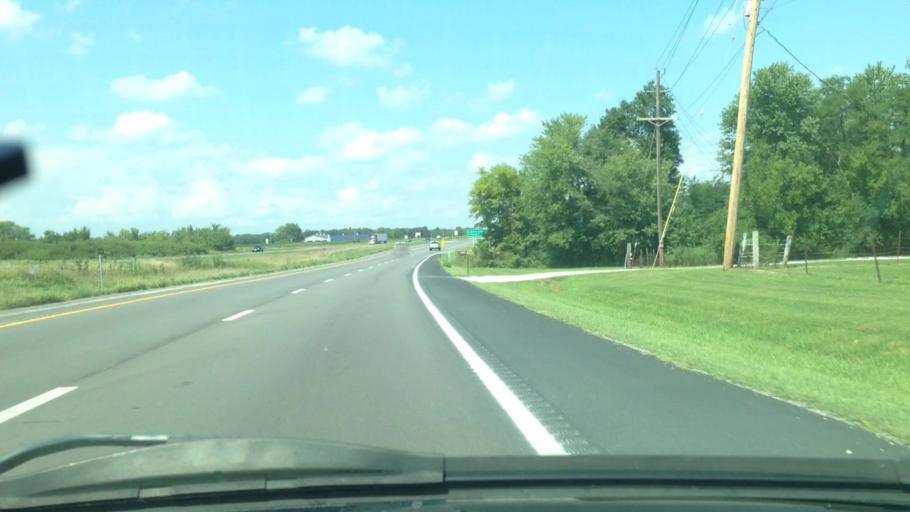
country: US
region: Missouri
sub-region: Lincoln County
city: Troy
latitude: 39.0808
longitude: -90.9723
